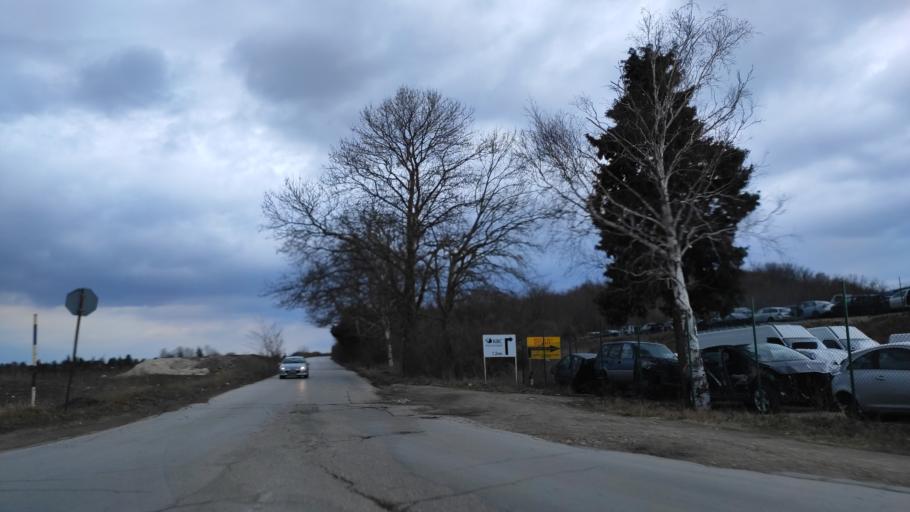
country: BG
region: Varna
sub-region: Obshtina Aksakovo
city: Aksakovo
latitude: 43.2297
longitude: 27.8055
